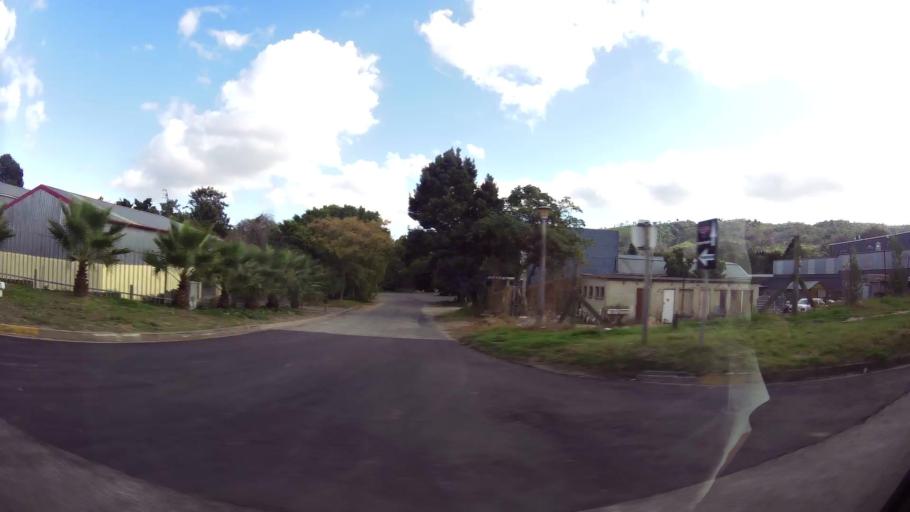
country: ZA
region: Western Cape
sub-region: Eden District Municipality
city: Knysna
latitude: -34.0444
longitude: 23.0759
